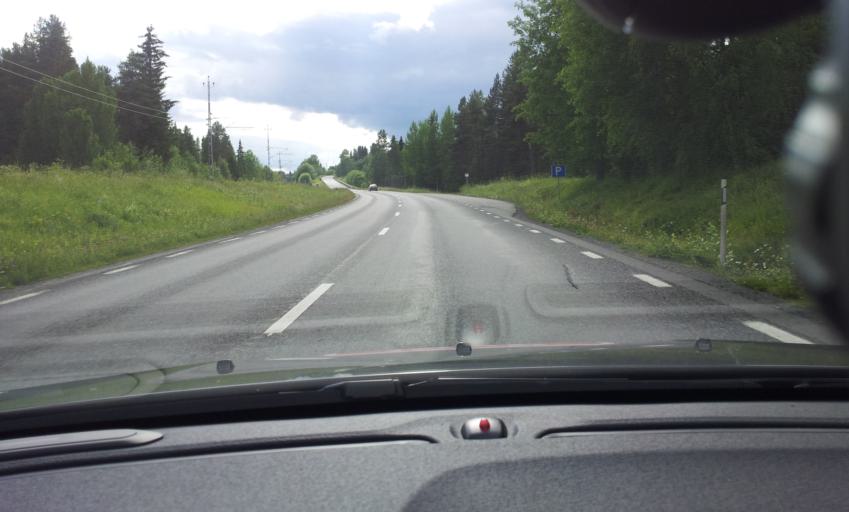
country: SE
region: Jaemtland
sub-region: Are Kommun
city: Jarpen
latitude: 63.3246
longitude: 13.3731
